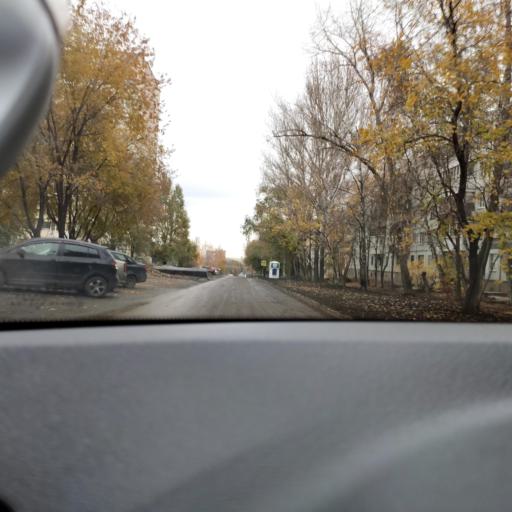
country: RU
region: Samara
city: Samara
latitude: 53.2198
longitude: 50.2209
